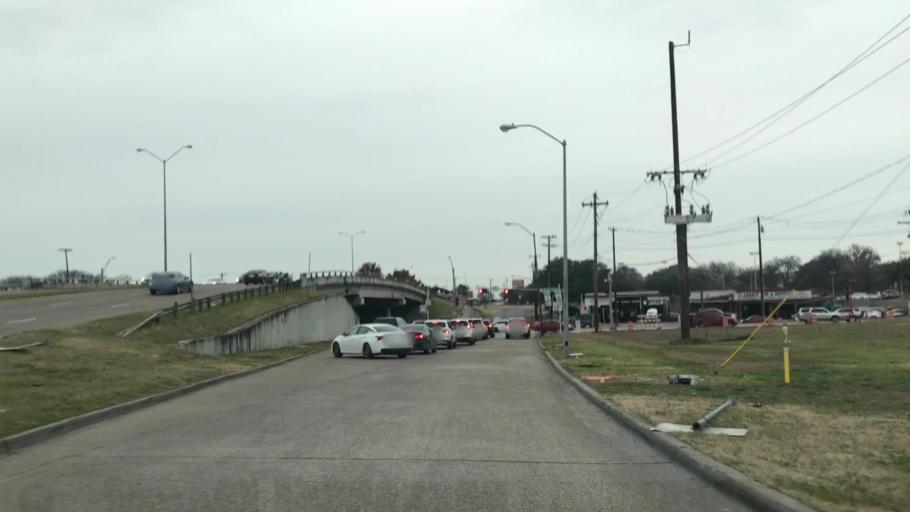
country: US
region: Texas
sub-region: Dallas County
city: University Park
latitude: 32.8603
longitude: -96.8542
